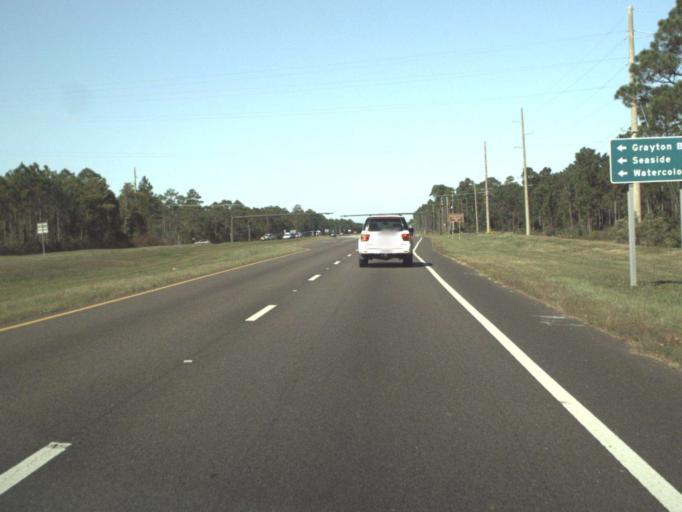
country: US
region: Florida
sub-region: Walton County
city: Seaside
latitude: 30.3588
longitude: -86.1532
